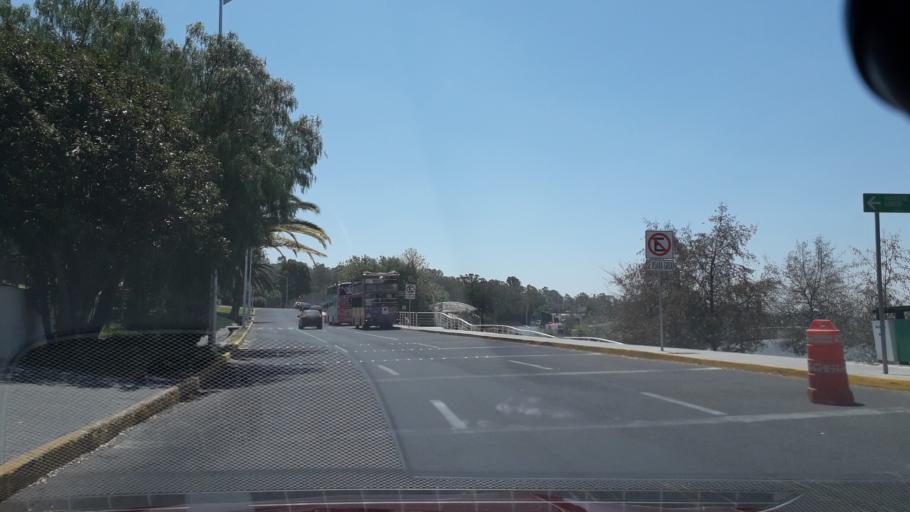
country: MX
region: Puebla
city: Puebla
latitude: 19.0570
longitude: -98.1879
